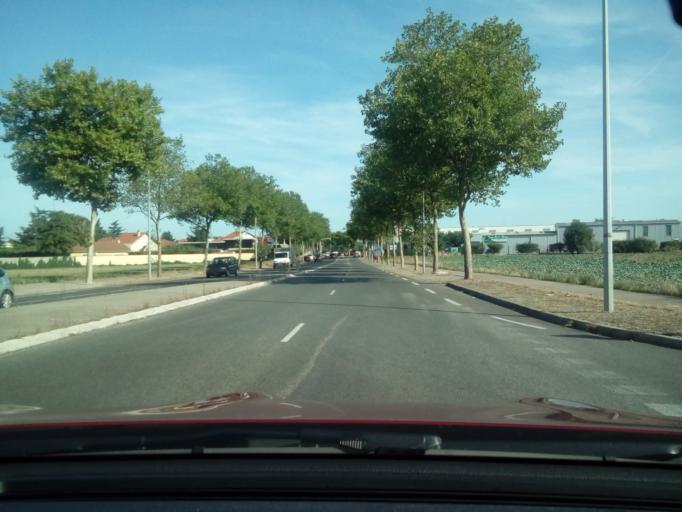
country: FR
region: Rhone-Alpes
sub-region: Departement du Rhone
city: Bron
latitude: 45.7450
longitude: 4.9373
